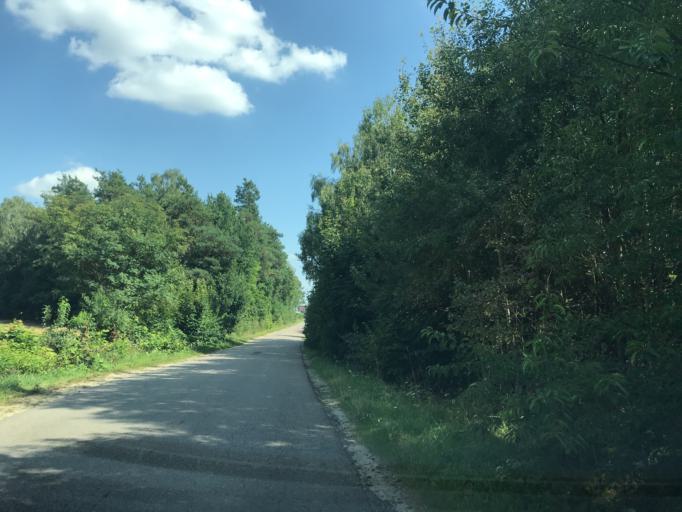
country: PL
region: Masovian Voivodeship
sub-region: Powiat zurominski
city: Lubowidz
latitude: 53.1577
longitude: 19.9120
